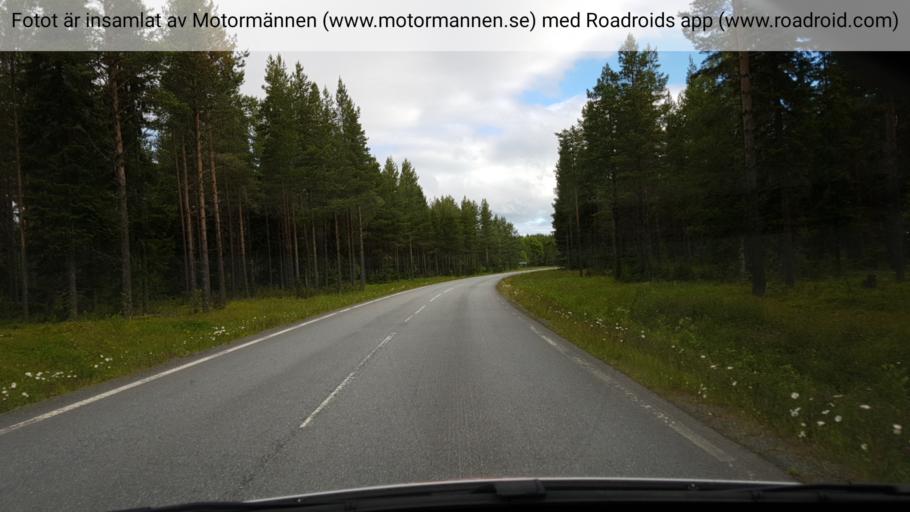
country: SE
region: Jaemtland
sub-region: Krokoms Kommun
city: Krokom
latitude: 63.2525
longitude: 14.4276
